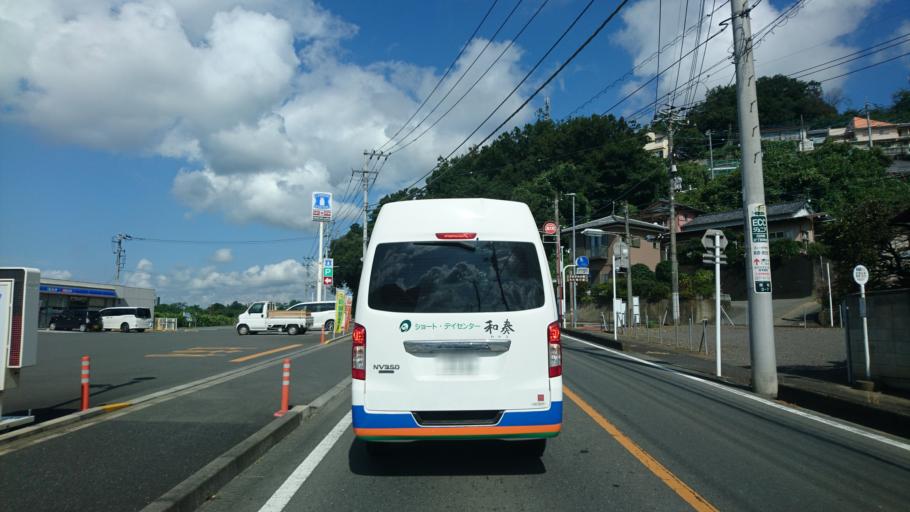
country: JP
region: Gunma
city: Kiryu
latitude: 36.4182
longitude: 139.3150
